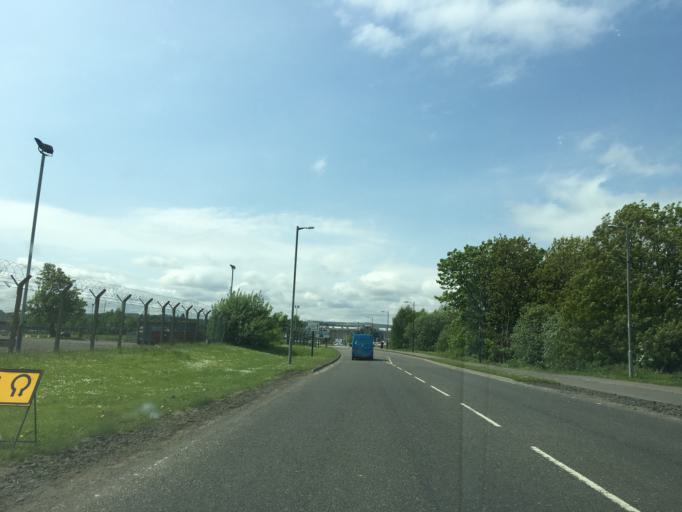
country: GB
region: Scotland
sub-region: Stirling
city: Stirling
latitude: 56.1193
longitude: -3.9250
